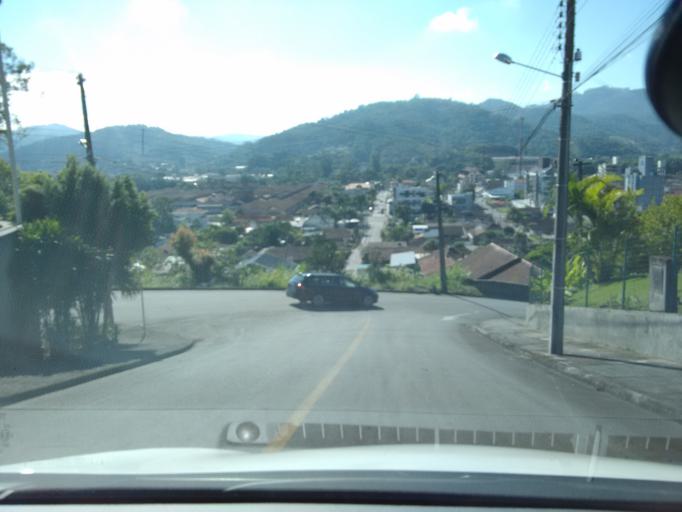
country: BR
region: Santa Catarina
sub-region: Pomerode
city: Pomerode
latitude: -26.7316
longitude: -49.1823
